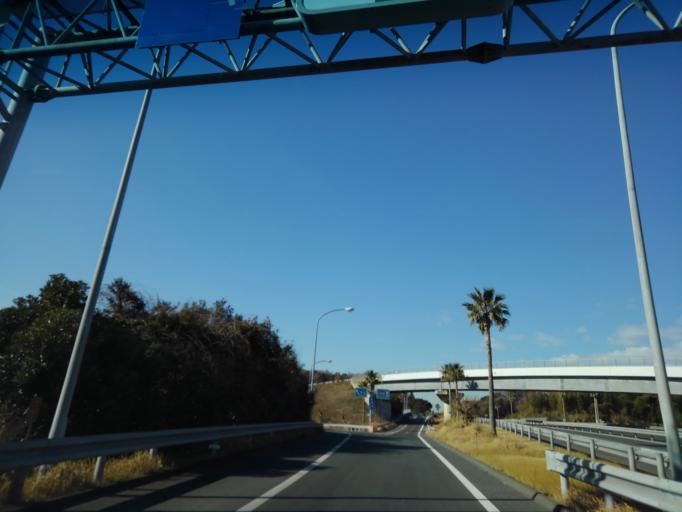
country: JP
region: Chiba
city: Kisarazu
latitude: 35.3501
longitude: 139.9222
